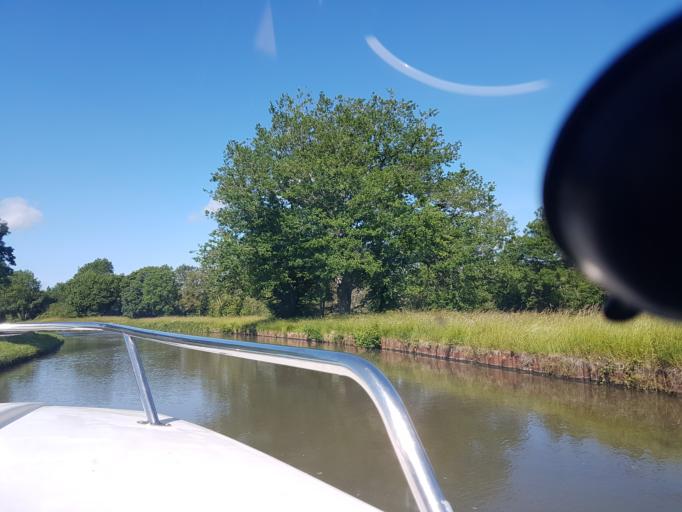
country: FR
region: Bourgogne
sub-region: Departement de la Nievre
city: Clamecy
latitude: 47.5400
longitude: 3.6029
